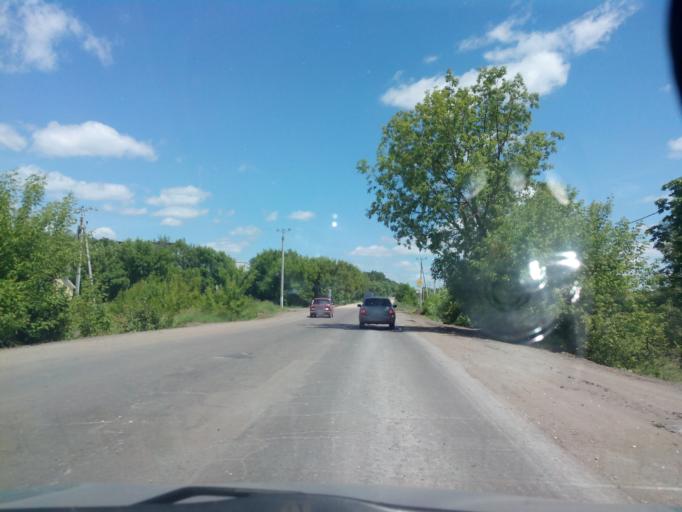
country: RU
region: Tambov
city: Zherdevka
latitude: 51.8155
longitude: 41.5107
